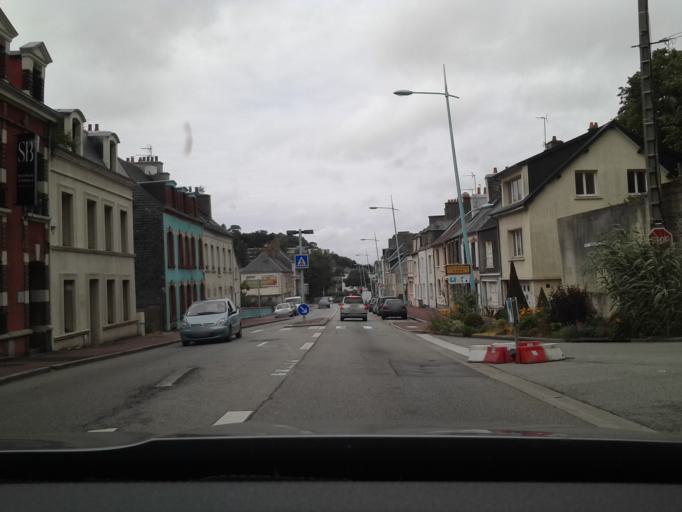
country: FR
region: Lower Normandy
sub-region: Departement de la Manche
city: Cherbourg-Octeville
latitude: 49.6265
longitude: -1.6173
